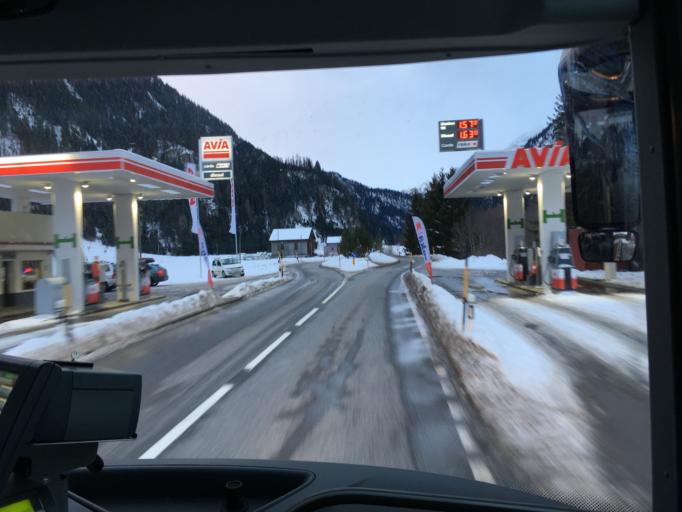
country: CH
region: Grisons
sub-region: Albula District
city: Tiefencastel
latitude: 46.5576
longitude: 9.6247
